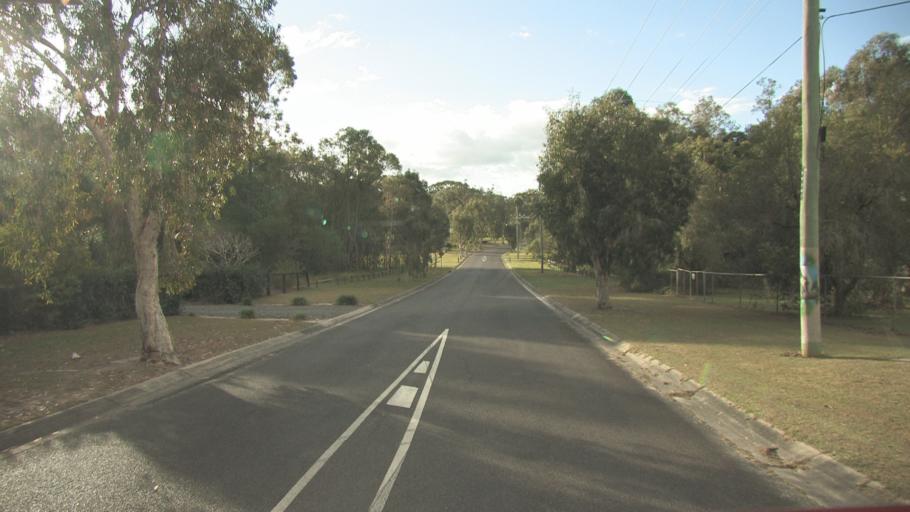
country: AU
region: Queensland
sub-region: Logan
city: Park Ridge South
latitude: -27.7033
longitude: 153.0206
